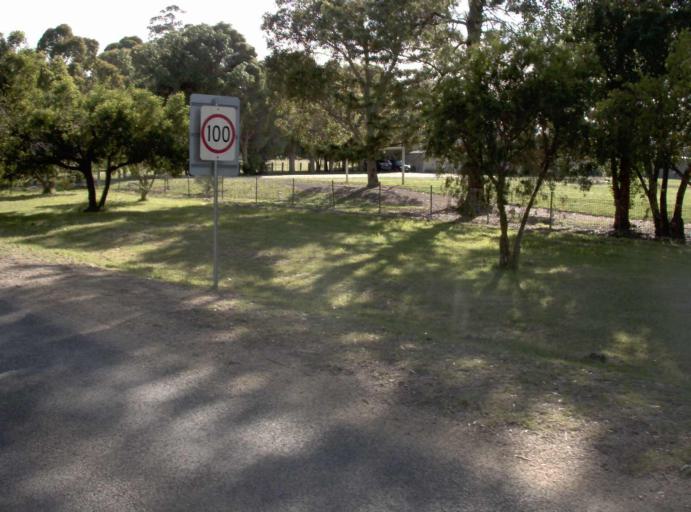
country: AU
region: Victoria
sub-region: East Gippsland
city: Lakes Entrance
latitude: -37.6970
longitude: 148.4649
